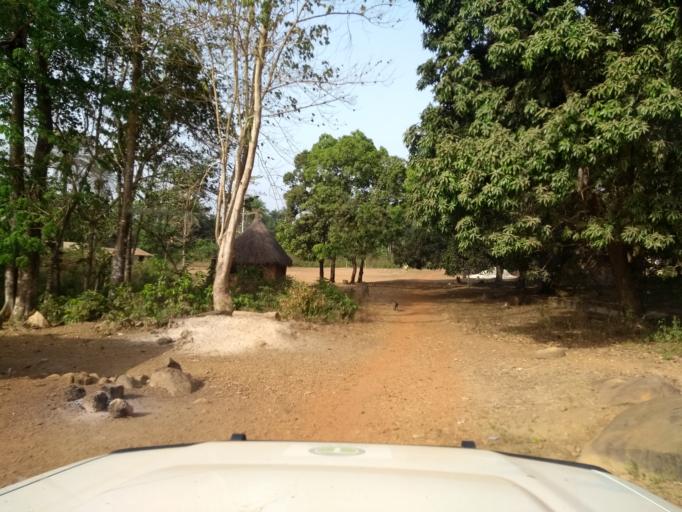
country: GN
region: Kindia
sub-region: Prefecture de Dubreka
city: Dubreka
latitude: 9.8152
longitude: -13.5597
